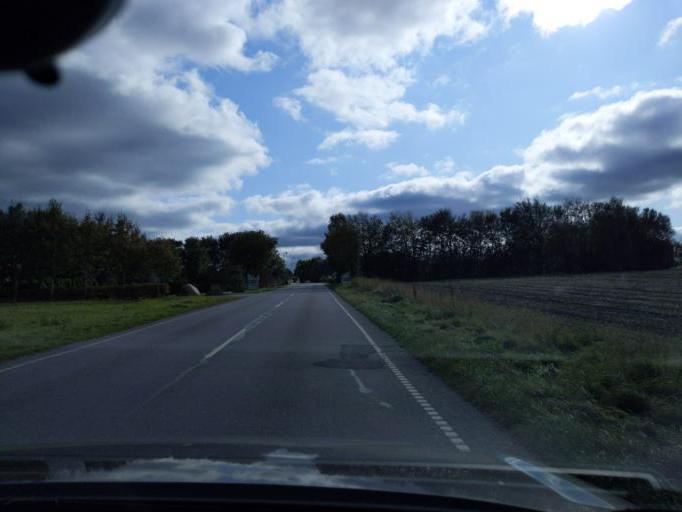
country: DK
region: North Denmark
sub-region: Mariagerfjord Kommune
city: Hobro
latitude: 56.5323
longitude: 9.7259
